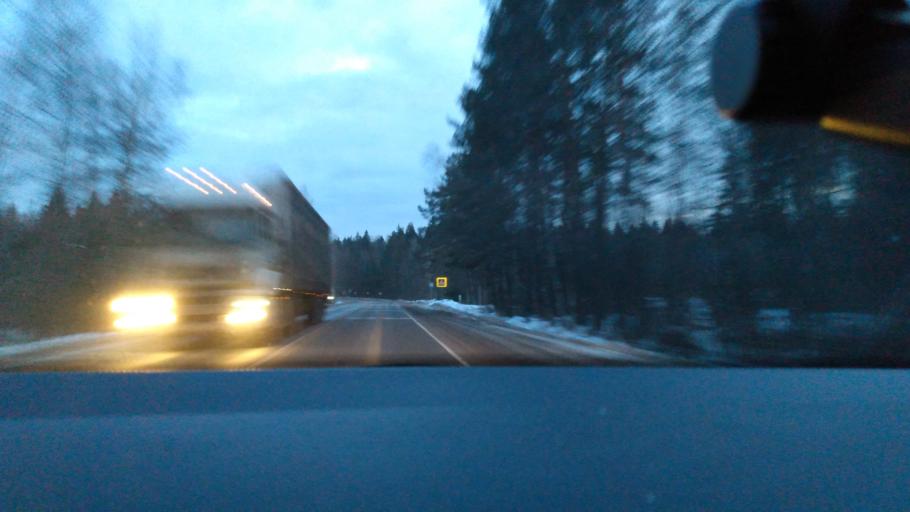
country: RU
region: Moskovskaya
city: Yegor'yevsk
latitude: 55.3173
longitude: 39.0730
